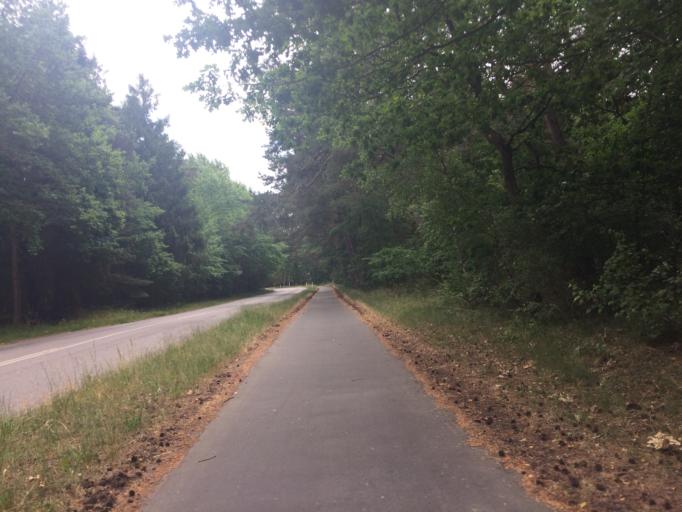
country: DK
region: Capital Region
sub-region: Bornholm Kommune
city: Ronne
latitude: 55.1689
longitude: 14.7127
